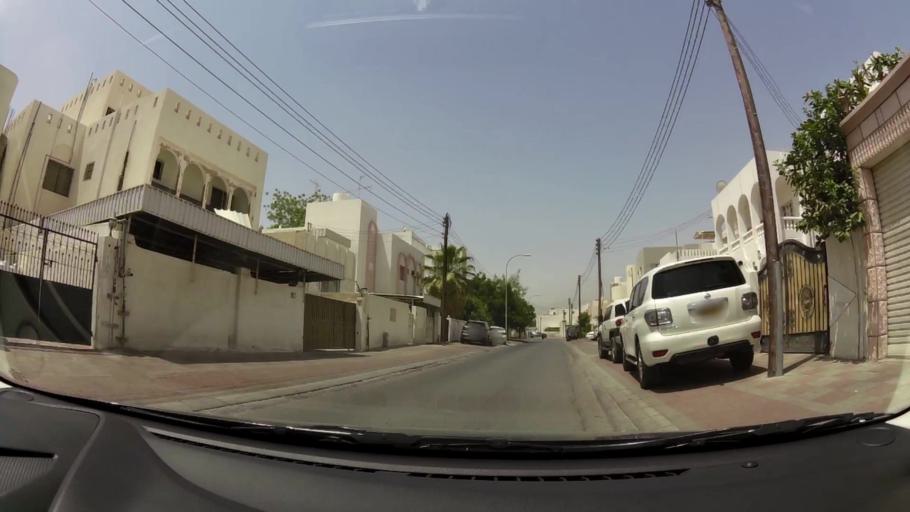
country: OM
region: Muhafazat Masqat
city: Bawshar
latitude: 23.5906
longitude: 58.4372
